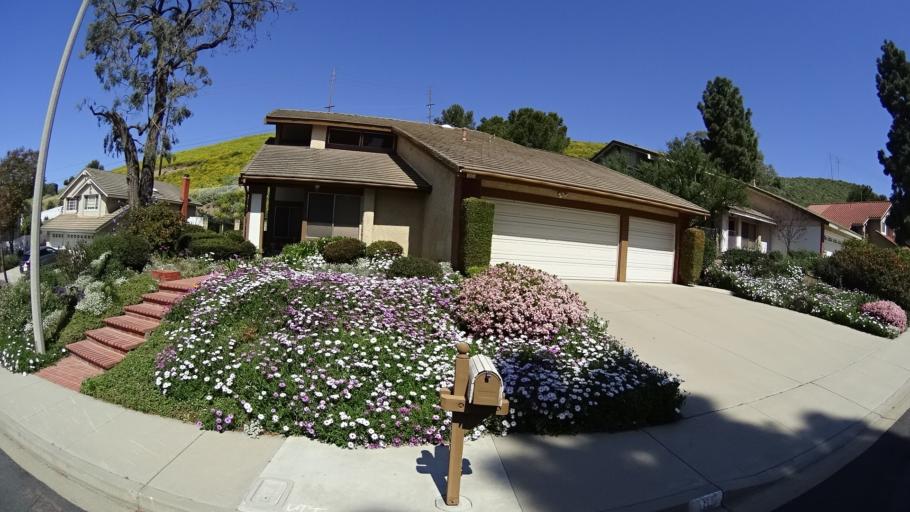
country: US
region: California
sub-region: Ventura County
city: Moorpark
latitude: 34.2298
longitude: -118.8674
